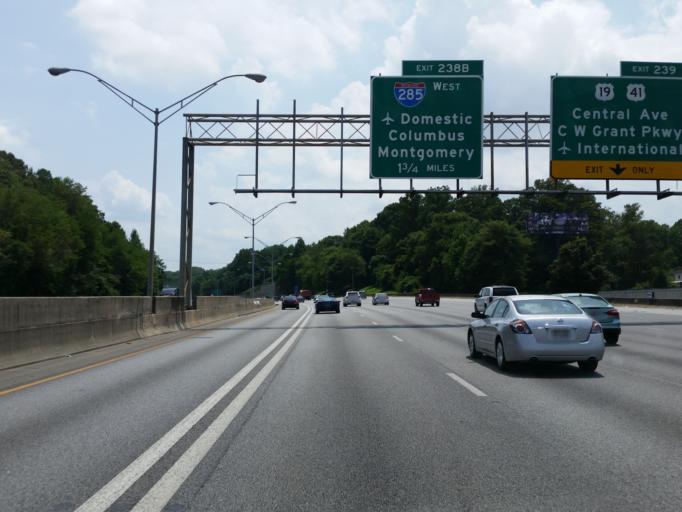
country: US
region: Georgia
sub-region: Fulton County
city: Hapeville
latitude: 33.6708
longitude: -84.3980
